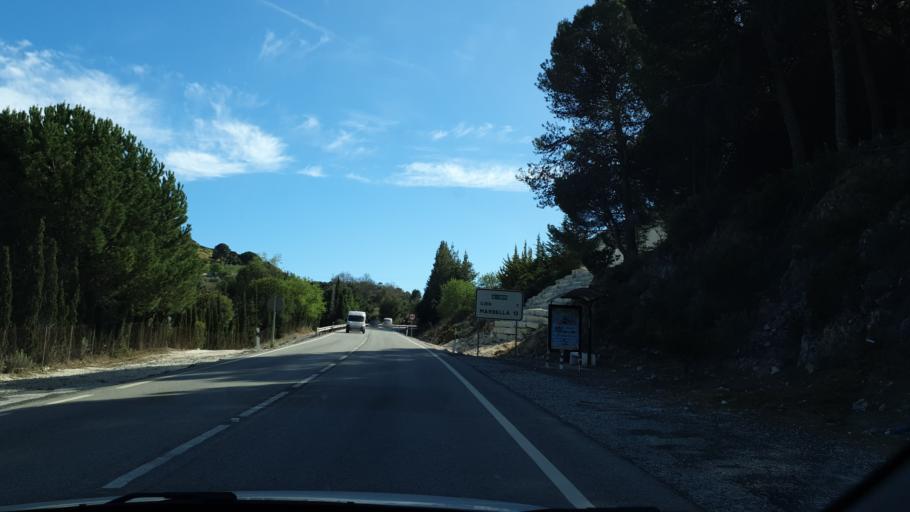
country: ES
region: Andalusia
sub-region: Provincia de Malaga
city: Ojen
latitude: 36.5893
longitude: -4.8520
